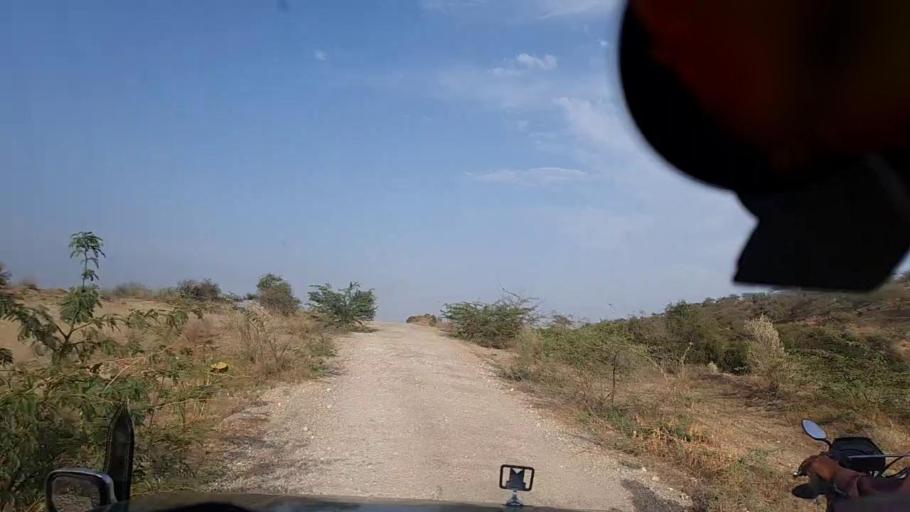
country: PK
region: Sindh
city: Diplo
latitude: 24.5584
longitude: 69.4751
